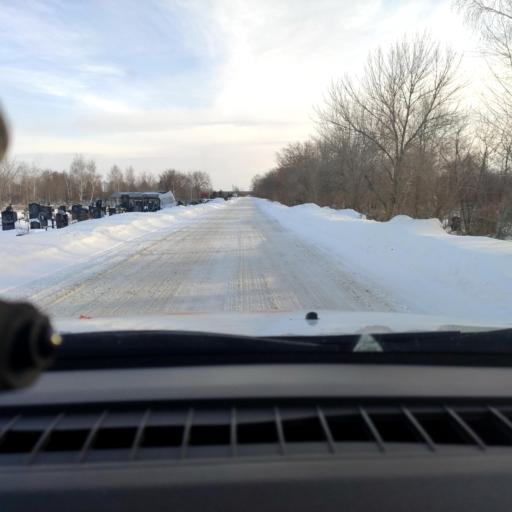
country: RU
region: Samara
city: Chapayevsk
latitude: 52.9912
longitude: 49.7434
